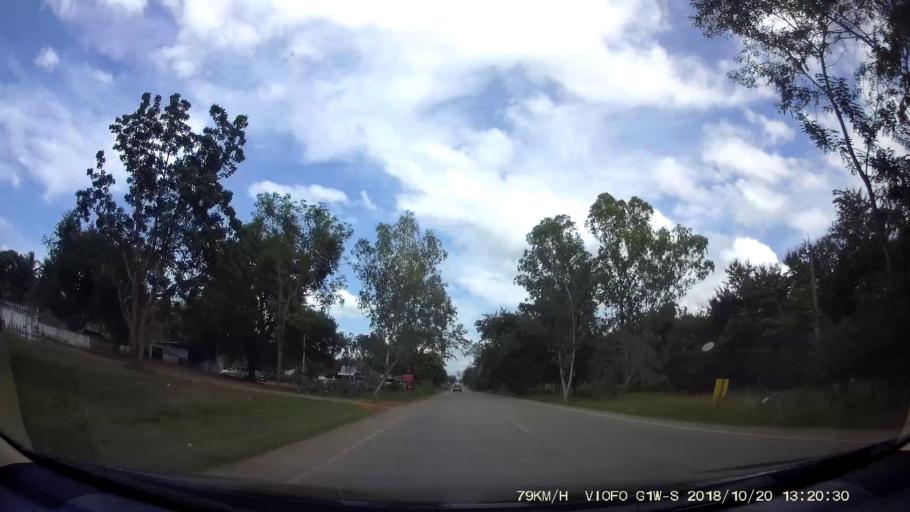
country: TH
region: Chaiyaphum
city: Khon San
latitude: 16.5489
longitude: 101.9045
